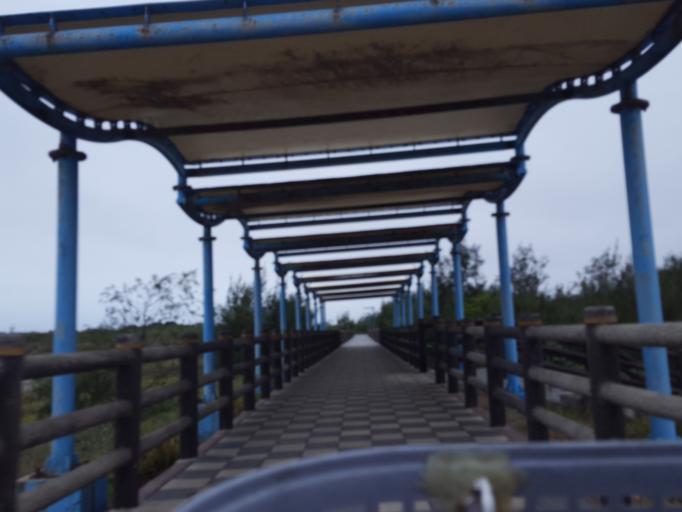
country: TW
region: Taiwan
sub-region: Hsinchu
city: Hsinchu
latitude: 24.8384
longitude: 120.9188
